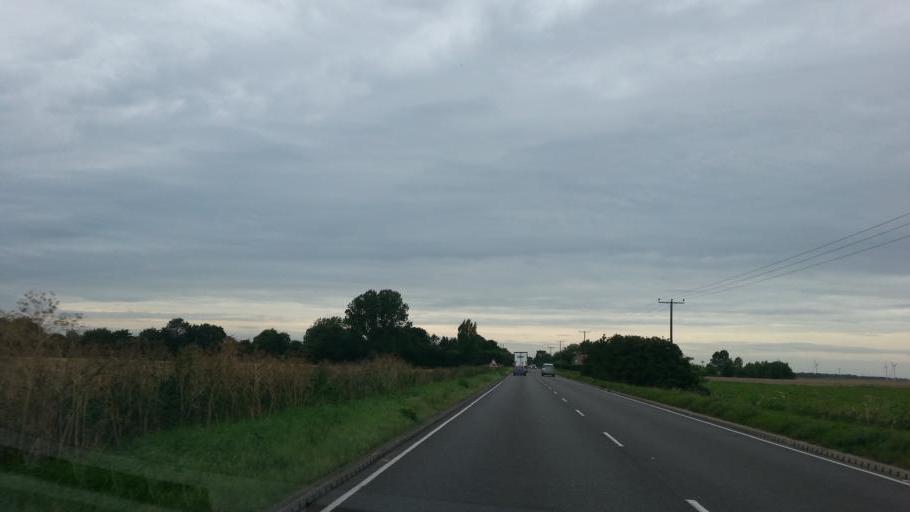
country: GB
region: England
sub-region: Cambridgeshire
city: March
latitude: 52.6123
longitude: 0.0177
